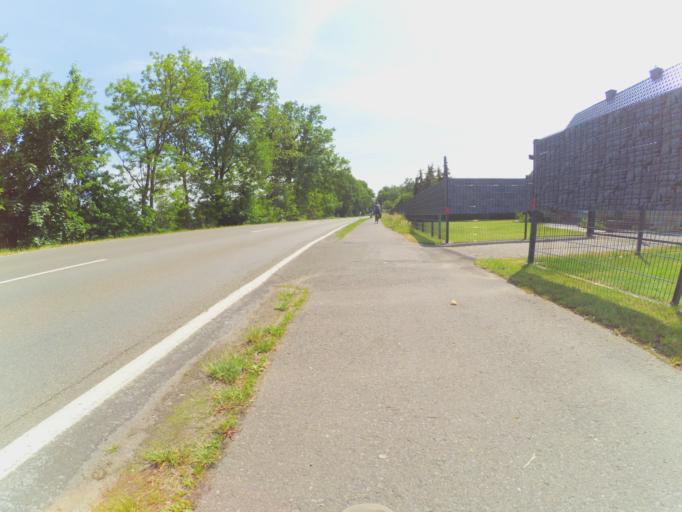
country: DE
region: North Rhine-Westphalia
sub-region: Regierungsbezirk Munster
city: Horstel
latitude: 52.3073
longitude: 7.6346
